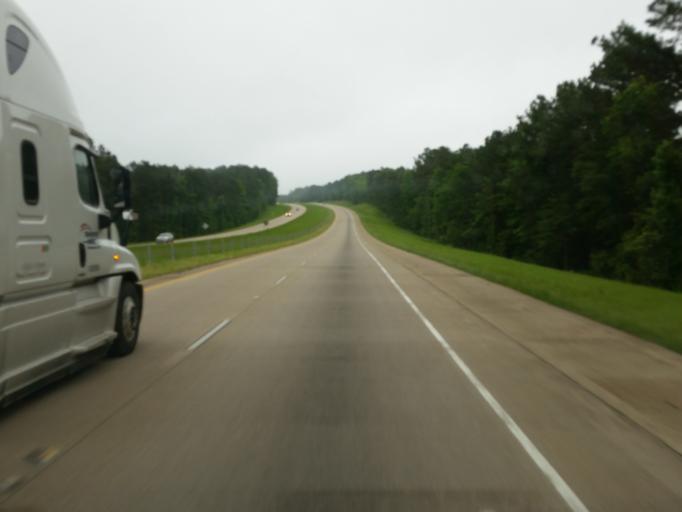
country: US
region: Louisiana
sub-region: Bienville Parish
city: Arcadia
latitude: 32.5614
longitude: -93.0320
